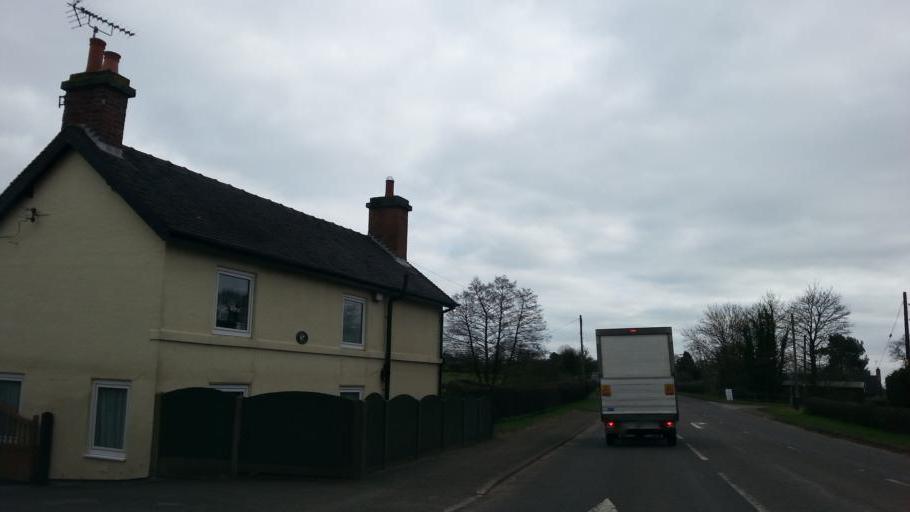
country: GB
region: England
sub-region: Staffordshire
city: Stafford
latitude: 52.8707
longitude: -2.0927
